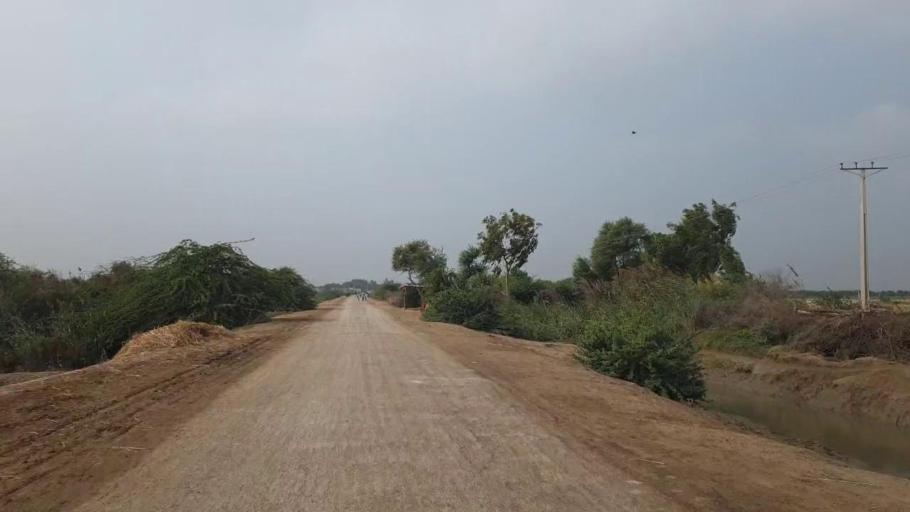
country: PK
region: Sindh
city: Matli
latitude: 24.9633
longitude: 68.5889
